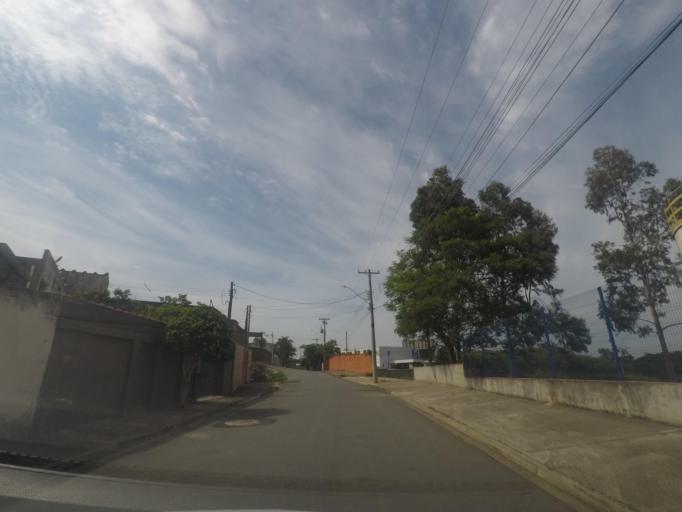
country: BR
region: Sao Paulo
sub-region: Sumare
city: Sumare
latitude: -22.8043
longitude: -47.2472
